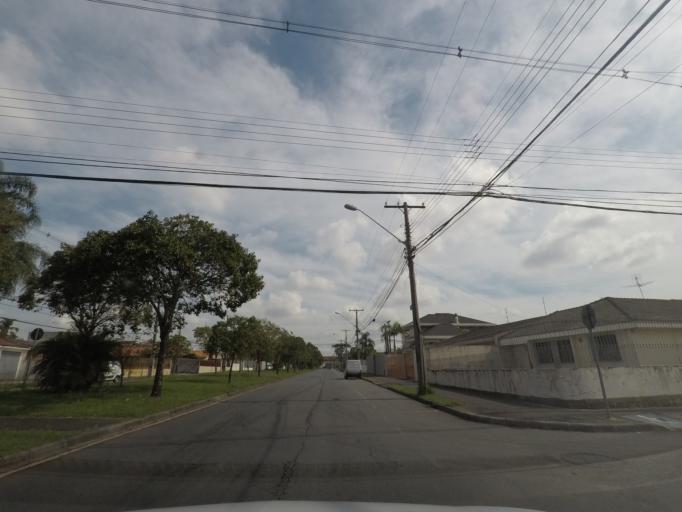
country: BR
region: Parana
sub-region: Pinhais
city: Pinhais
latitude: -25.4718
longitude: -49.2074
